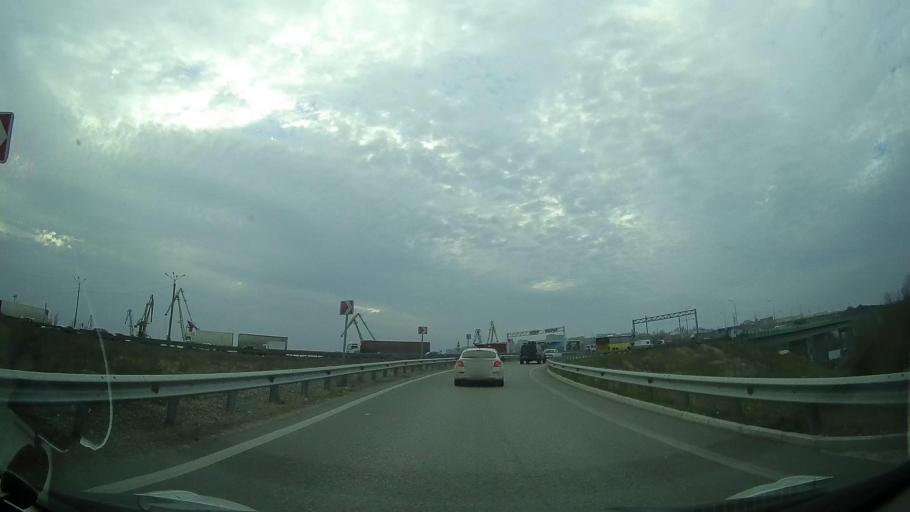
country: RU
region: Rostov
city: Aksay
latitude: 47.2399
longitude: 39.8558
